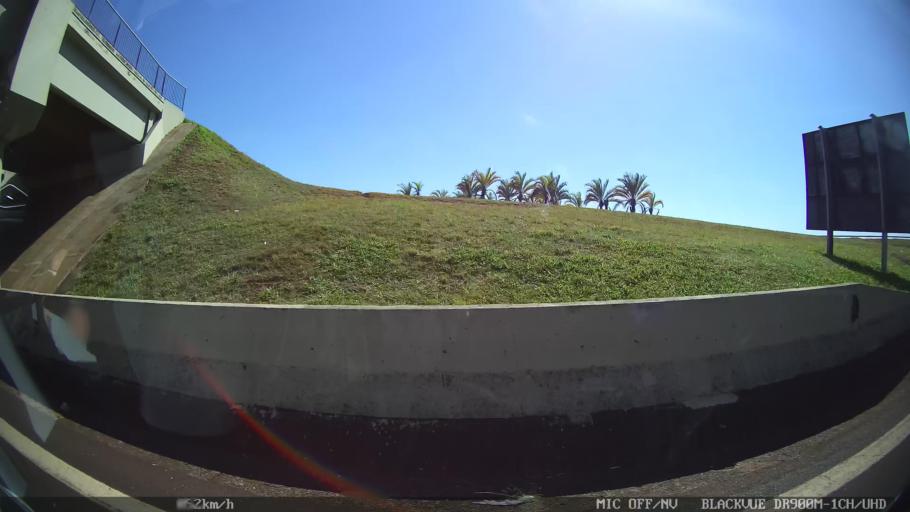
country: BR
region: Sao Paulo
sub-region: Franca
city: Franca
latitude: -20.5615
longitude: -47.4129
